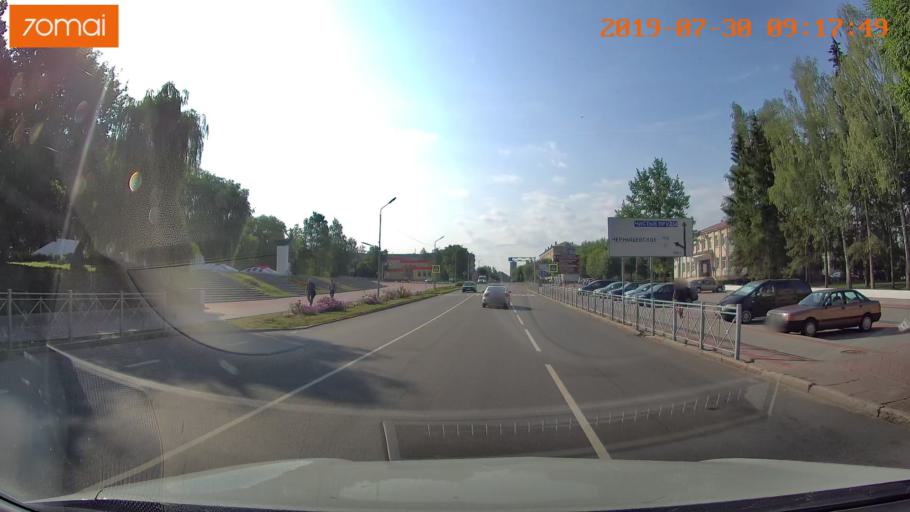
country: RU
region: Kaliningrad
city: Nesterov
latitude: 54.6322
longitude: 22.5706
